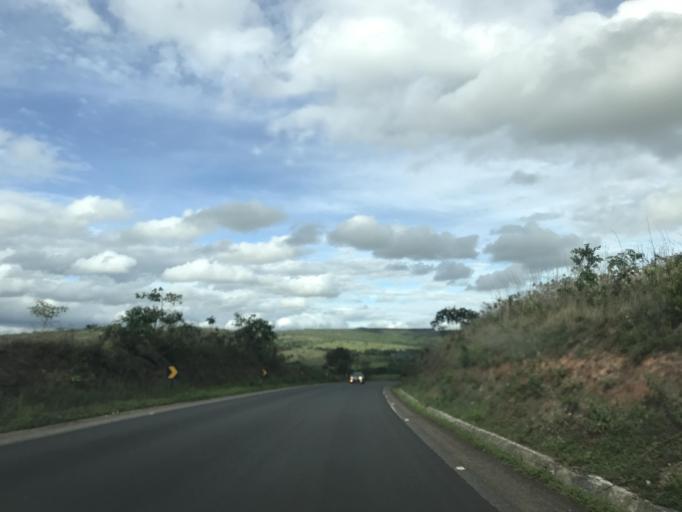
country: BR
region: Goias
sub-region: Vianopolis
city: Vianopolis
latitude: -16.9479
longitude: -48.5891
